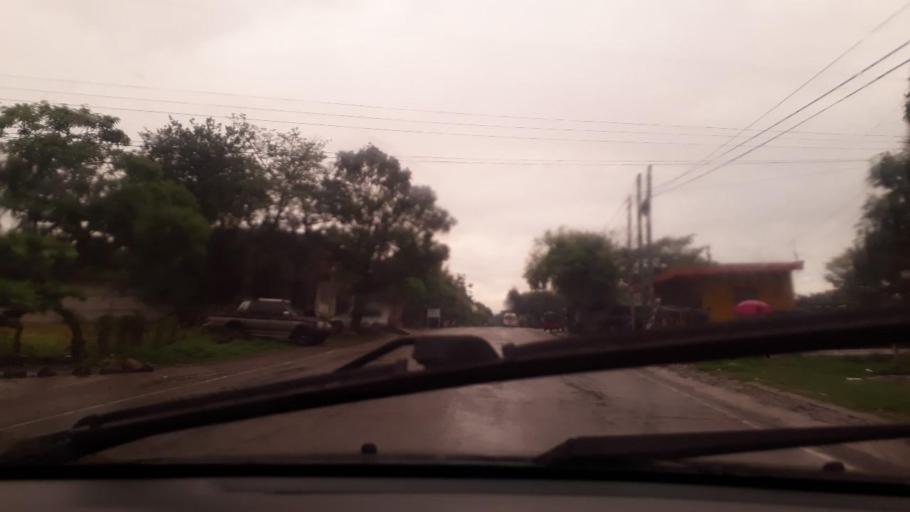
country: GT
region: Jutiapa
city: Comapa
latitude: 14.0579
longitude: -89.9415
